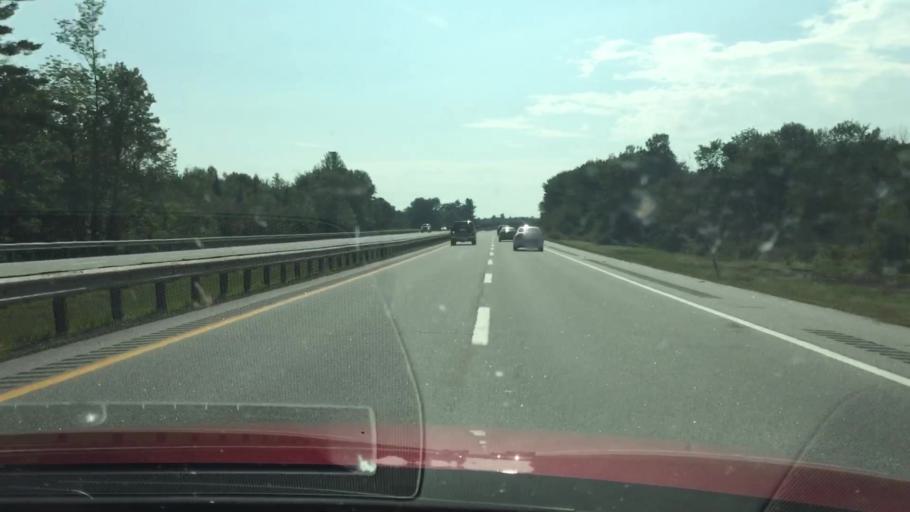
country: US
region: Maine
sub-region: Kennebec County
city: Monmouth
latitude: 44.1301
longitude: -69.9593
